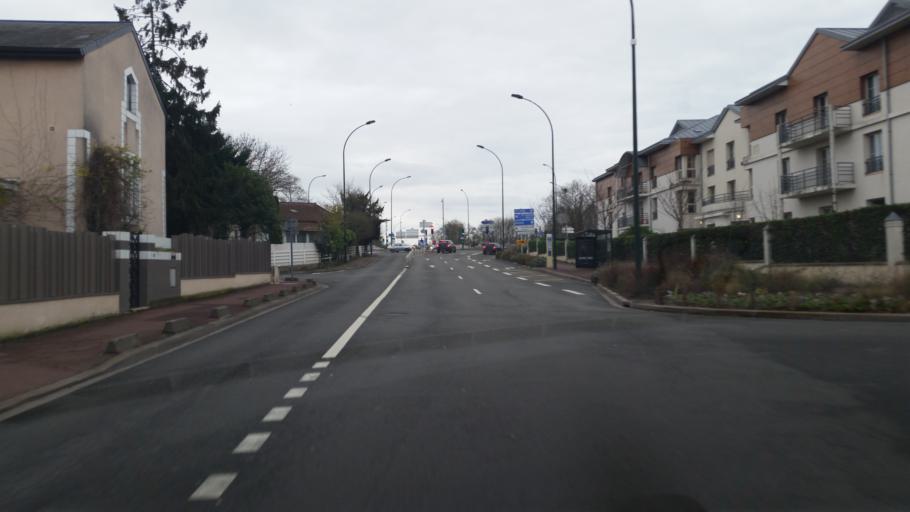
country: FR
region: Ile-de-France
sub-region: Departement des Hauts-de-Seine
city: Vaucresson
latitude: 48.8335
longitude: 2.1537
